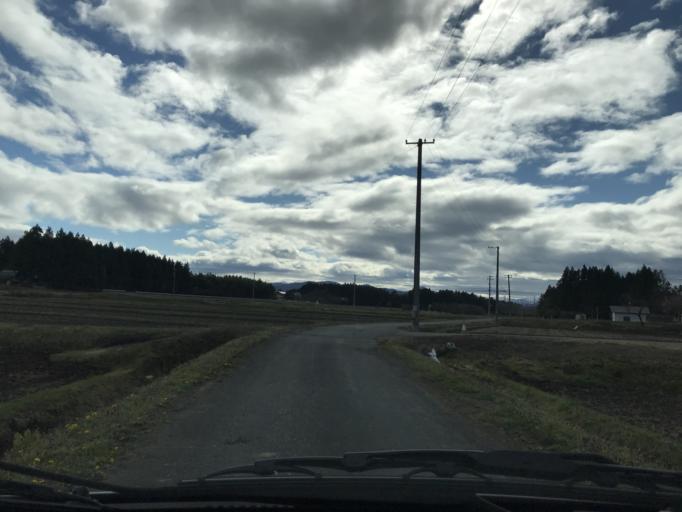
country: JP
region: Iwate
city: Mizusawa
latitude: 39.1095
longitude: 141.1051
